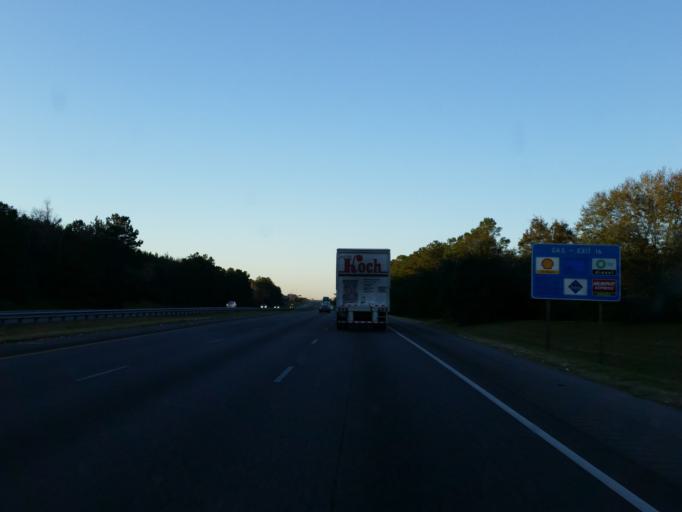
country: US
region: Georgia
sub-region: Lowndes County
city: Valdosta
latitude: 30.8007
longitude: -83.3066
